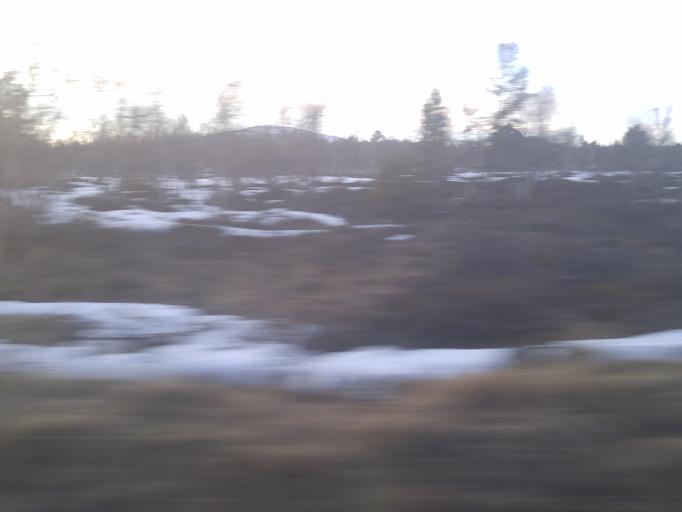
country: NO
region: Oppland
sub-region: Dovre
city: Dombas
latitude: 62.1020
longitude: 9.2100
